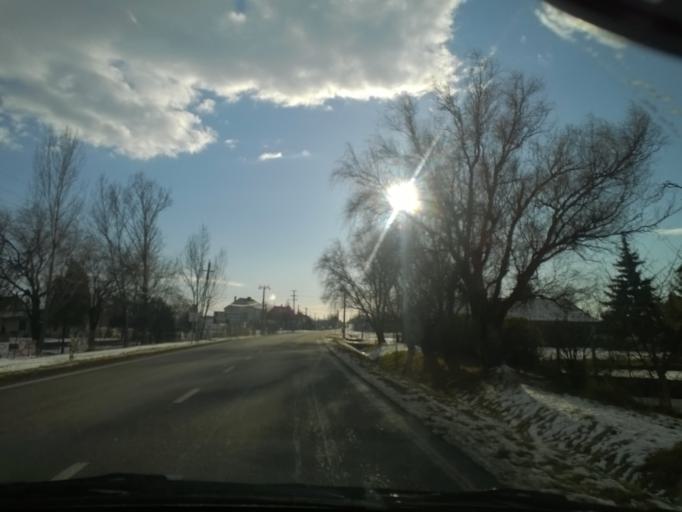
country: HU
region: Fejer
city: Polgardi
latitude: 47.0494
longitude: 18.3024
